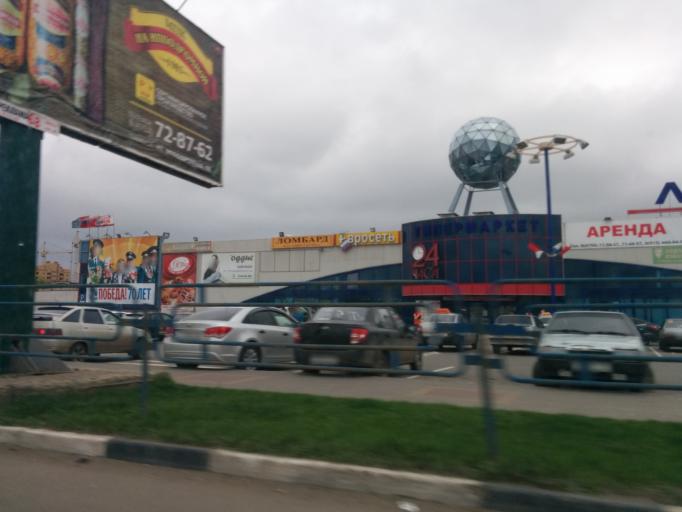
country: RU
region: Tambov
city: Tambov
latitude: 52.7237
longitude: 41.4365
